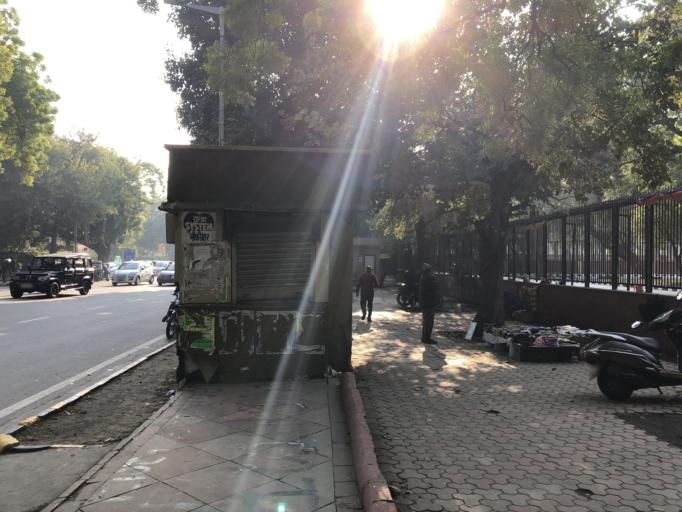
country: IN
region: NCT
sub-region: New Delhi
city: New Delhi
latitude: 28.6210
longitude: 77.2107
